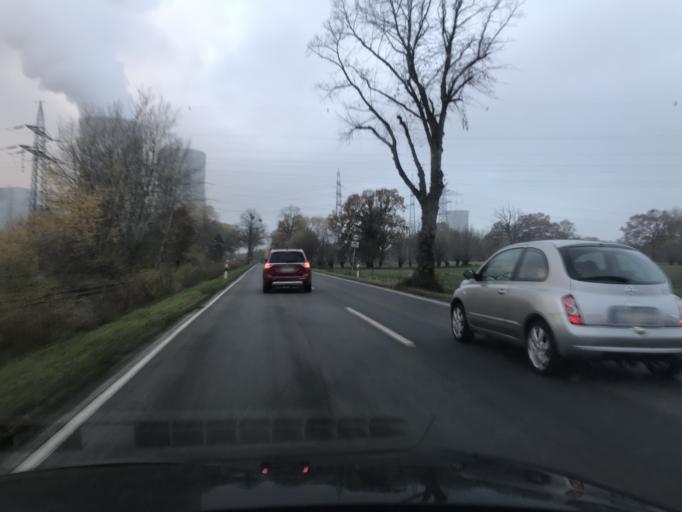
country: DE
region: North Rhine-Westphalia
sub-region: Regierungsbezirk Arnsberg
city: Welver
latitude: 51.6735
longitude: 7.9855
